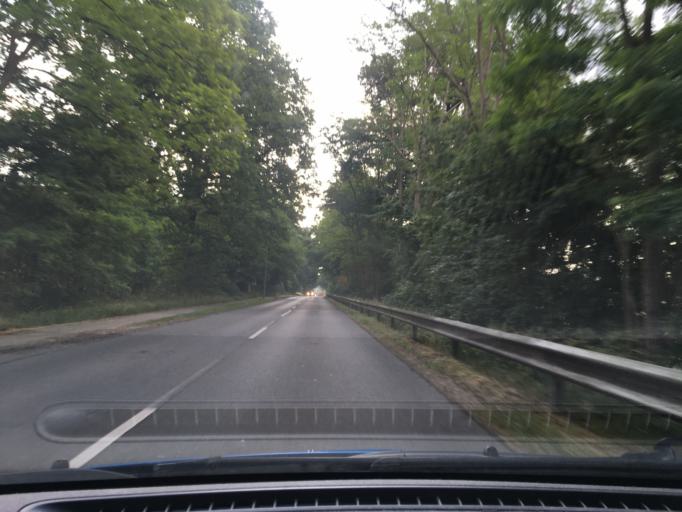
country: DE
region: Lower Saxony
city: Buchholz in der Nordheide
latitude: 53.3206
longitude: 9.8396
